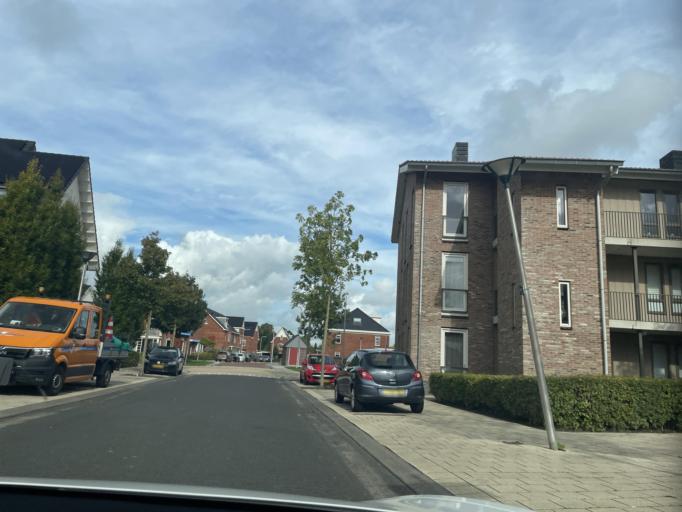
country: NL
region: South Holland
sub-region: Gemeente Albrandswaard
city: Rhoon
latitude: 51.8534
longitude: 4.4330
